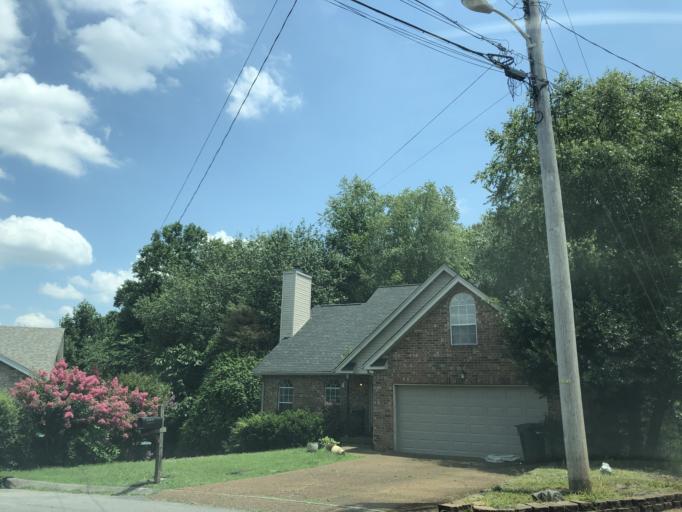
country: US
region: Tennessee
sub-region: Williamson County
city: Brentwood Estates
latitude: 36.0206
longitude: -86.7212
